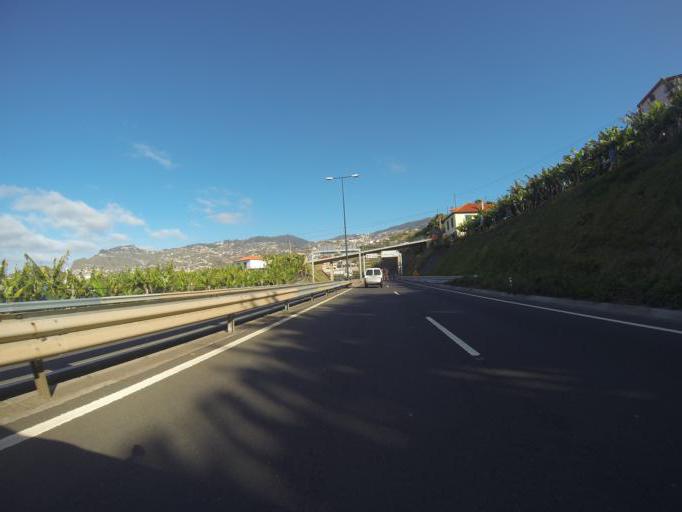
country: PT
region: Madeira
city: Camara de Lobos
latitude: 32.6529
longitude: -16.9618
